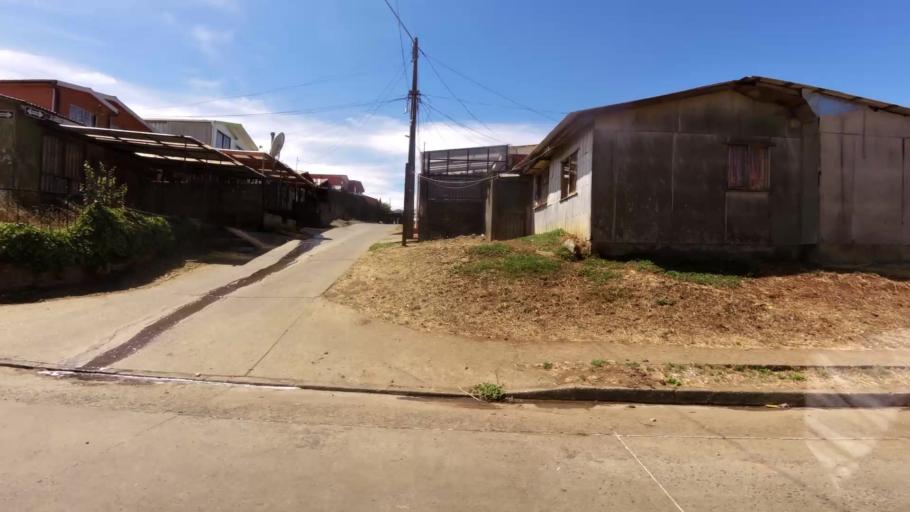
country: CL
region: Biobio
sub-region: Provincia de Concepcion
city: Talcahuano
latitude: -36.7137
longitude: -73.1403
